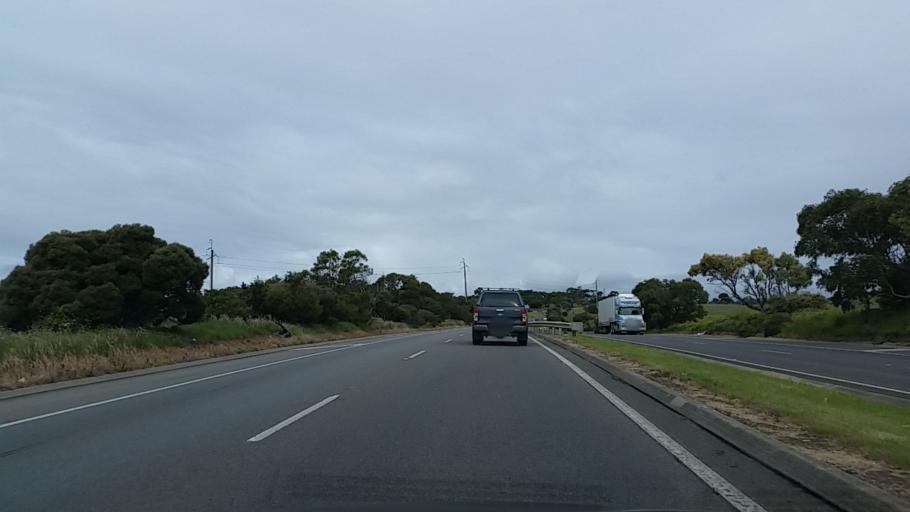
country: AU
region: South Australia
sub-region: Adelaide Hills
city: Seacliff
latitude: -35.0482
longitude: 138.5327
